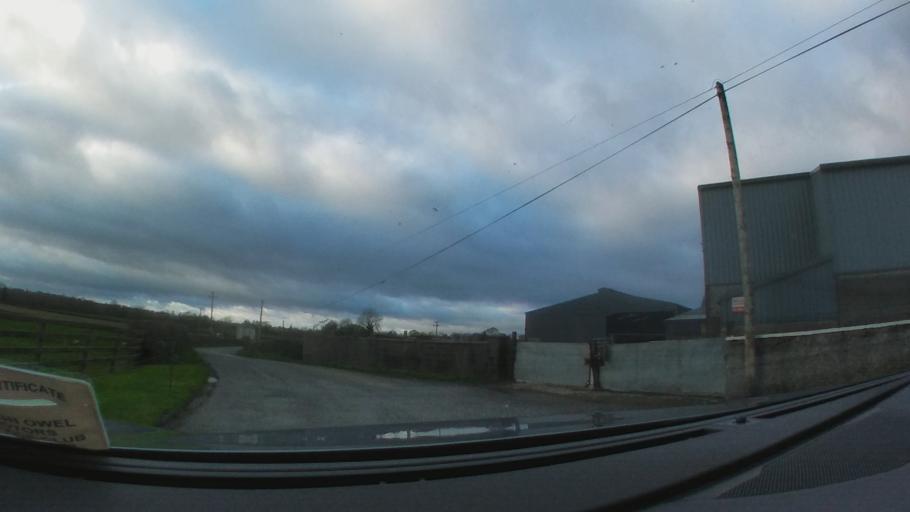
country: IE
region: Leinster
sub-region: Kilkenny
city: Thomastown
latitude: 52.5832
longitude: -7.1645
